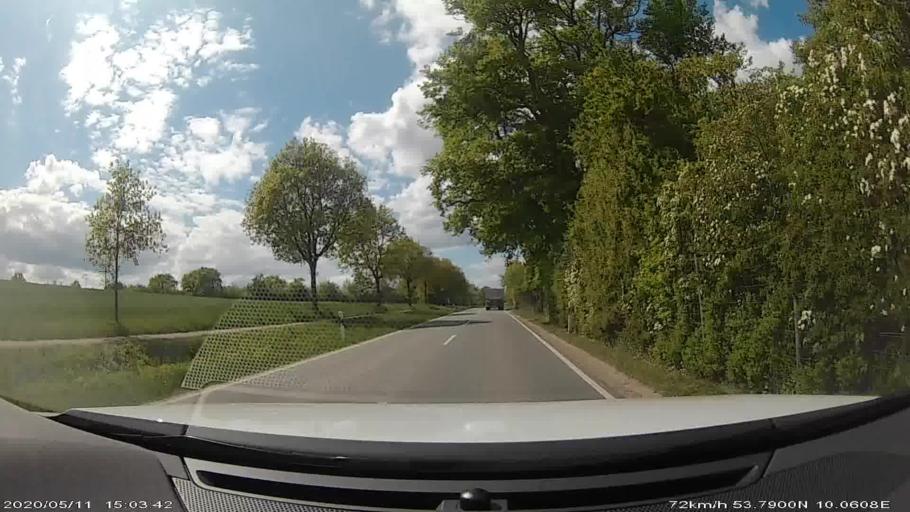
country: DE
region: Schleswig-Holstein
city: Kisdorf
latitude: 53.7918
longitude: 10.0489
